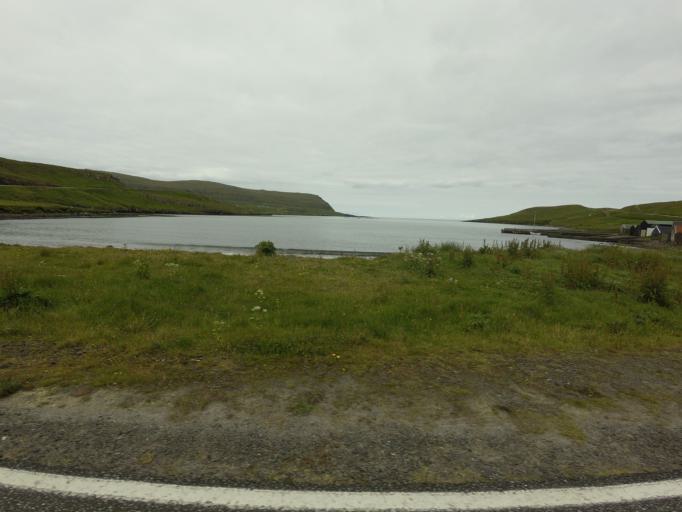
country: FO
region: Suduroy
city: Tvoroyri
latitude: 61.5339
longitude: -6.8116
